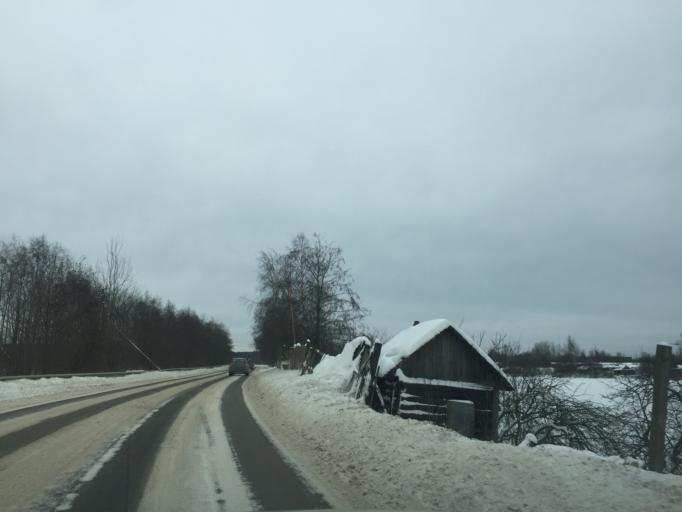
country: RU
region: Leningrad
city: Imeni Sverdlova
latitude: 59.7903
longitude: 30.7012
